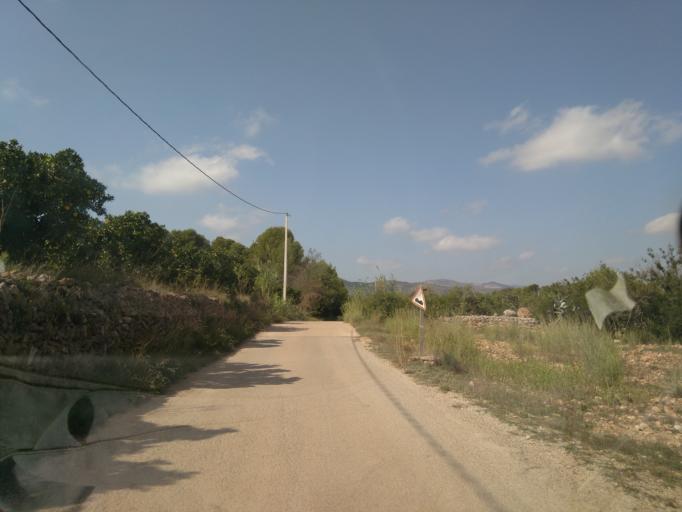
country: ES
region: Valencia
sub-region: Provincia de Valencia
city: Tous
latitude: 39.1670
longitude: -0.5791
